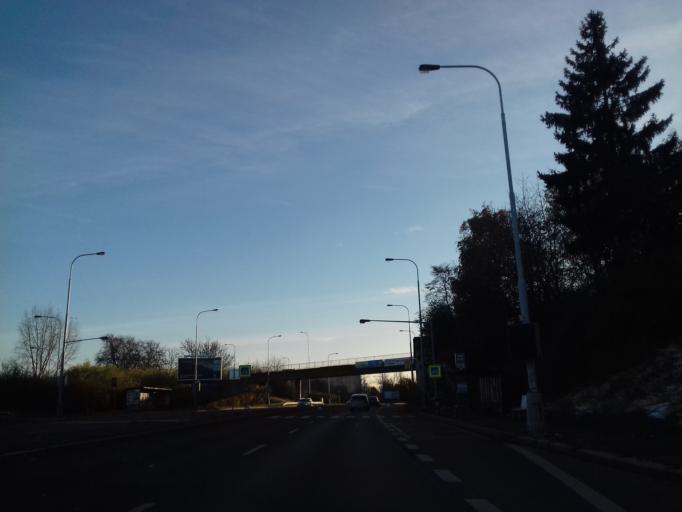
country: CZ
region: Central Bohemia
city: Hostivice
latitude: 50.0513
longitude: 14.3094
